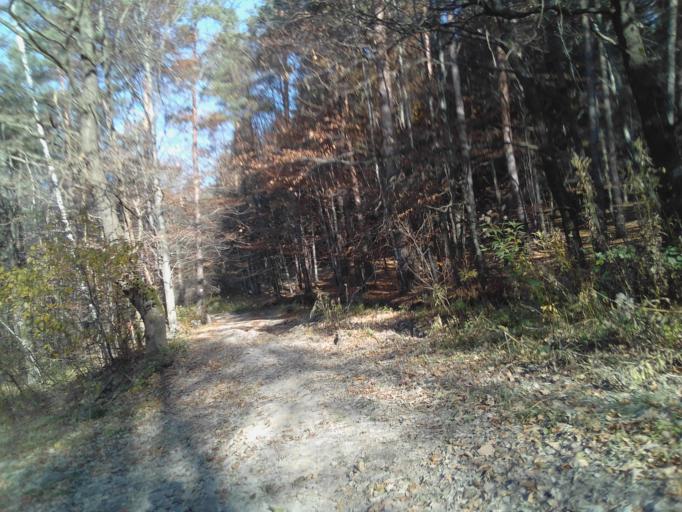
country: PL
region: Subcarpathian Voivodeship
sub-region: Powiat strzyzowski
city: Wysoka Strzyzowska
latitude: 49.8004
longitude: 21.7267
